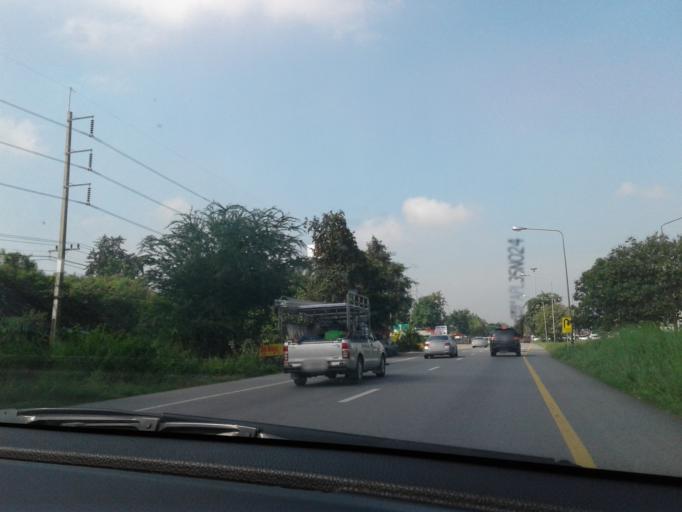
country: TH
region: Nakhon Pathom
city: Nakhon Pathom
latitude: 13.7978
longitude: 99.9720
